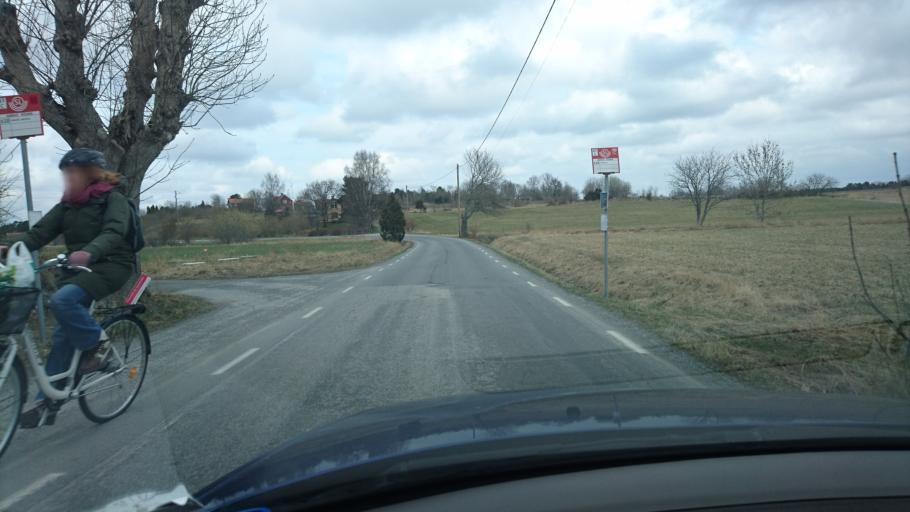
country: SE
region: Stockholm
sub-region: Norrtalje Kommun
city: Bjorko
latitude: 59.8031
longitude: 18.9570
